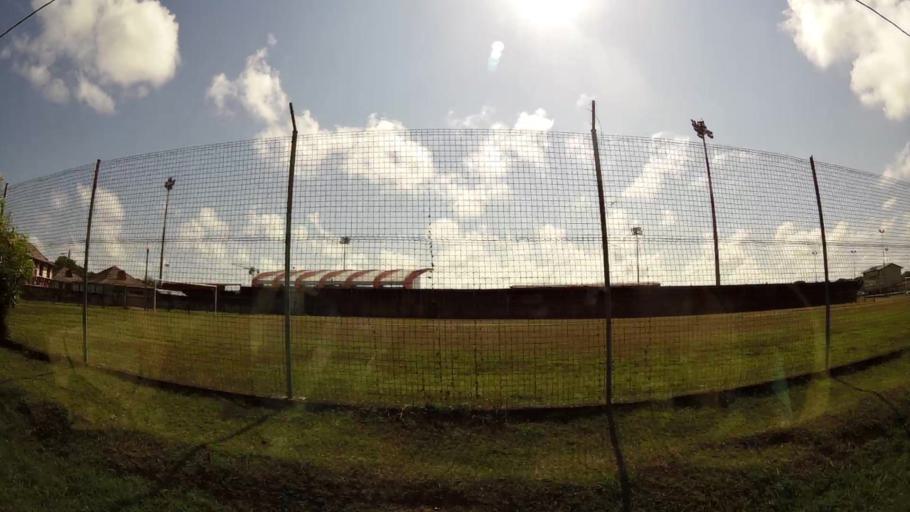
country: GF
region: Guyane
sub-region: Guyane
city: Cayenne
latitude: 4.9329
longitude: -52.3129
